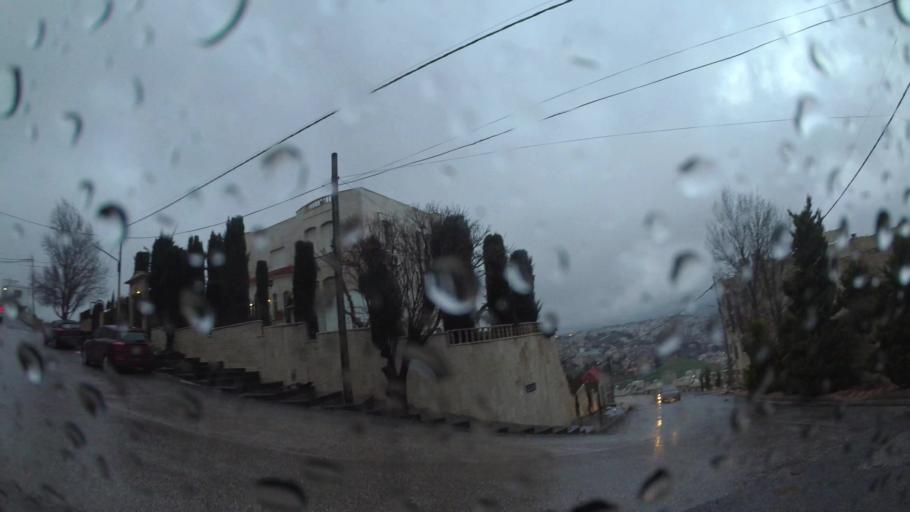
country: JO
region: Amman
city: Al Jubayhah
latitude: 32.0320
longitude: 35.8468
